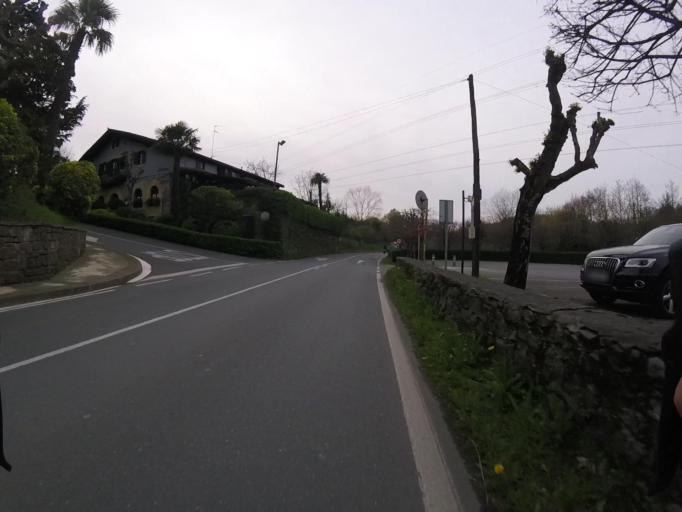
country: ES
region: Basque Country
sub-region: Provincia de Guipuzcoa
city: Errenteria
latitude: 43.2932
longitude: -1.8660
